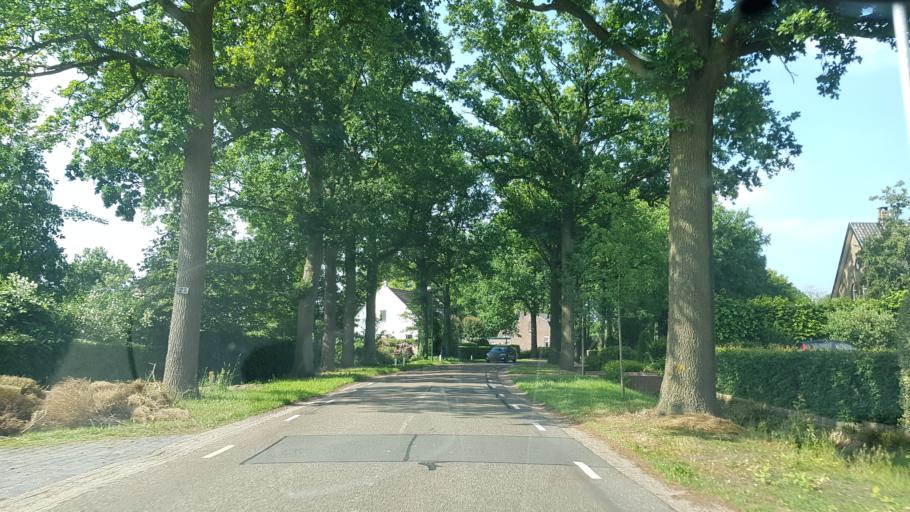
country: NL
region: North Brabant
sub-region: Gemeente Breda
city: Hoge Vucht
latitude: 51.6164
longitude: 4.8182
